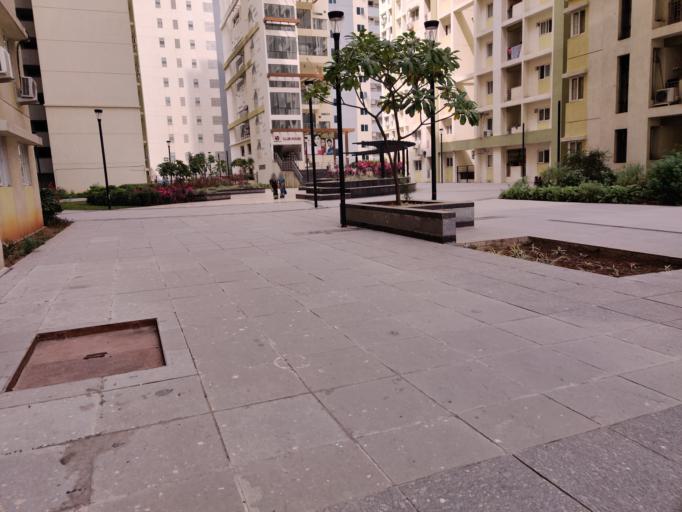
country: IN
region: Telangana
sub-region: Medak
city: Serilingampalle
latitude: 17.4229
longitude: 78.3411
